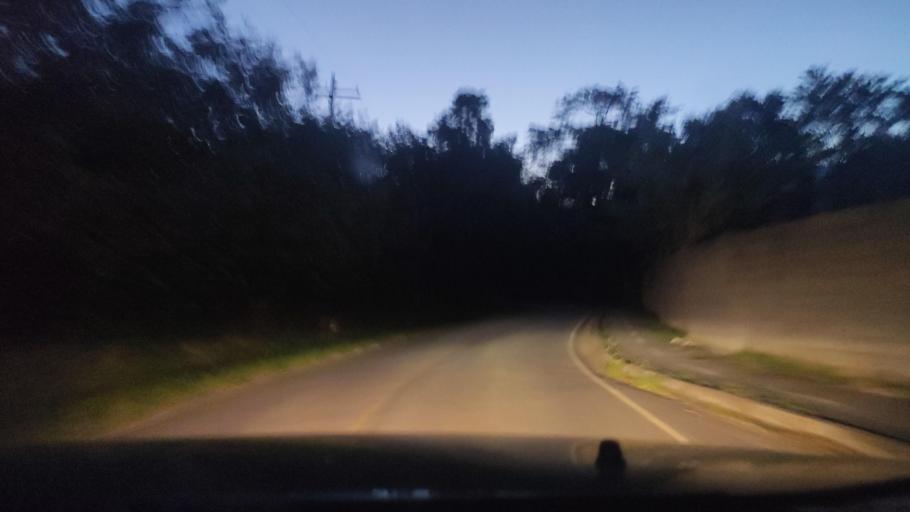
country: BR
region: Minas Gerais
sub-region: Paraisopolis
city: Paraisopolis
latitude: -22.7033
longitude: -45.7589
